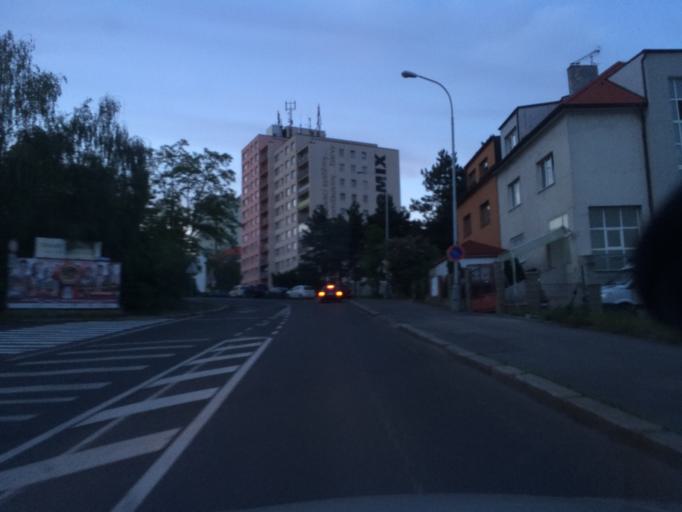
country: CZ
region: Praha
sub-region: Praha 4
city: Hodkovicky
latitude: 50.0417
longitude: 14.4593
